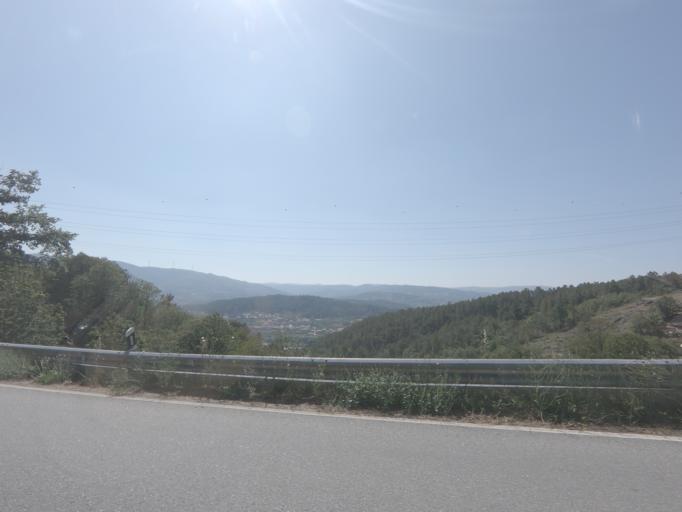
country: PT
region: Viseu
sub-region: Tarouca
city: Tarouca
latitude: 41.0366
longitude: -7.7408
